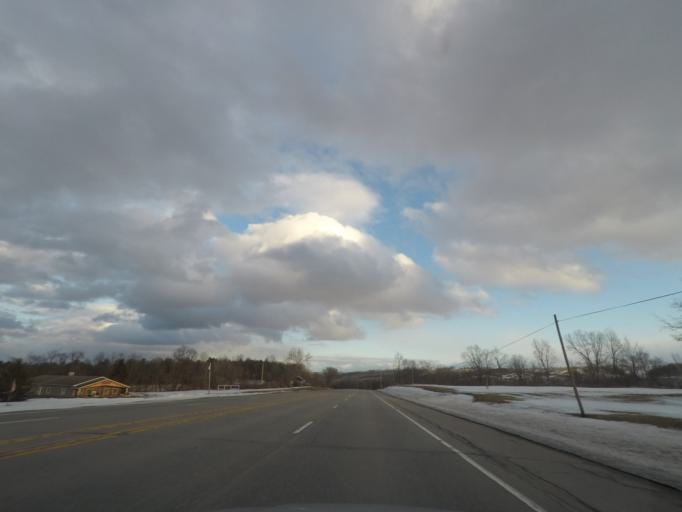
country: US
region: New York
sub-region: Herkimer County
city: Dolgeville
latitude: 43.0137
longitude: -74.7707
